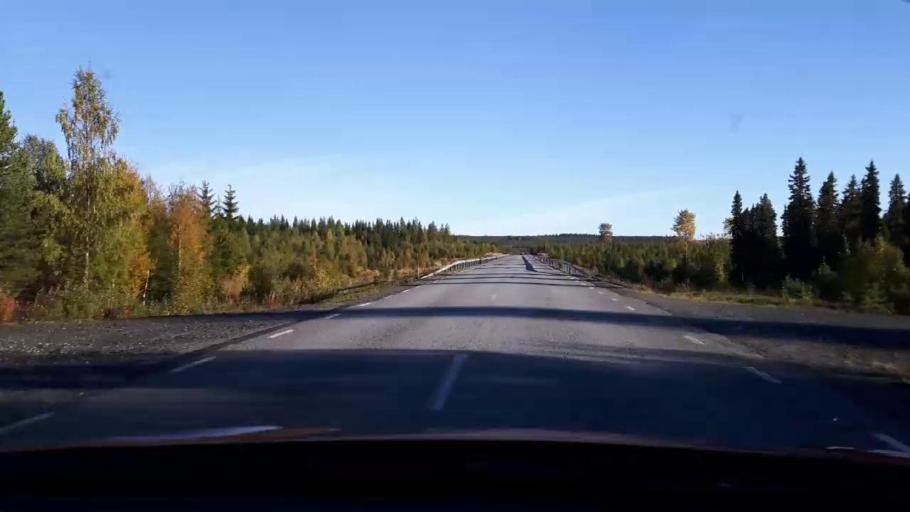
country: SE
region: Jaemtland
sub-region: OEstersunds Kommun
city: Lit
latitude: 63.7750
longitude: 14.7126
